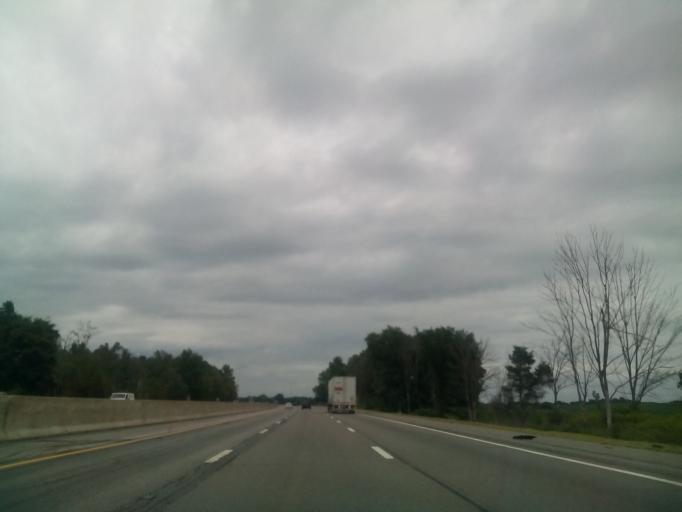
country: US
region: Ohio
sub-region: Lorain County
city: South Amherst
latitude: 41.3459
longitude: -82.3251
